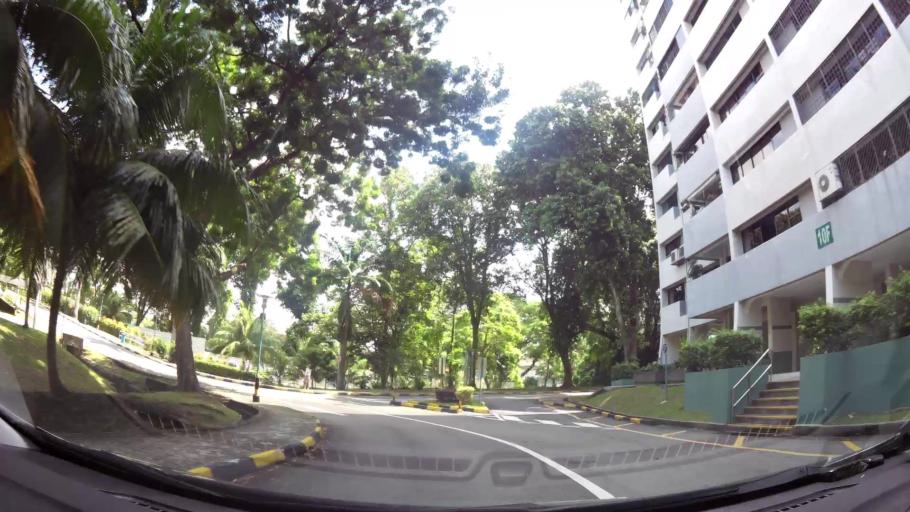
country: SG
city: Singapore
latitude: 1.3419
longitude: 103.8419
